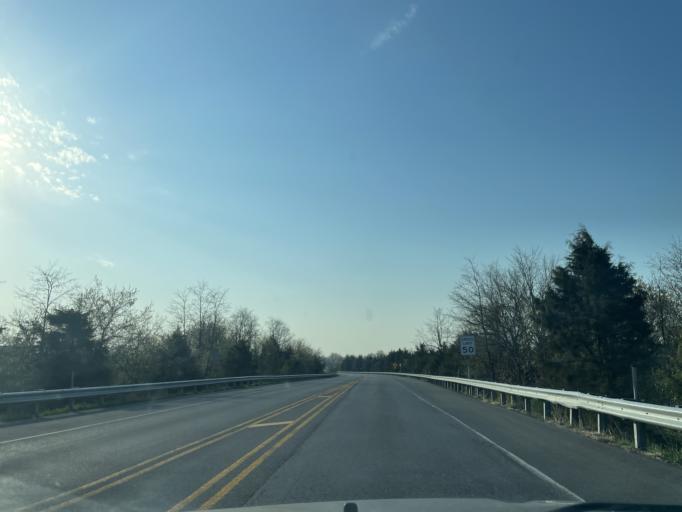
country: US
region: Maryland
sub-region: Washington County
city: Williamsport
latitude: 39.5839
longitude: -77.8123
